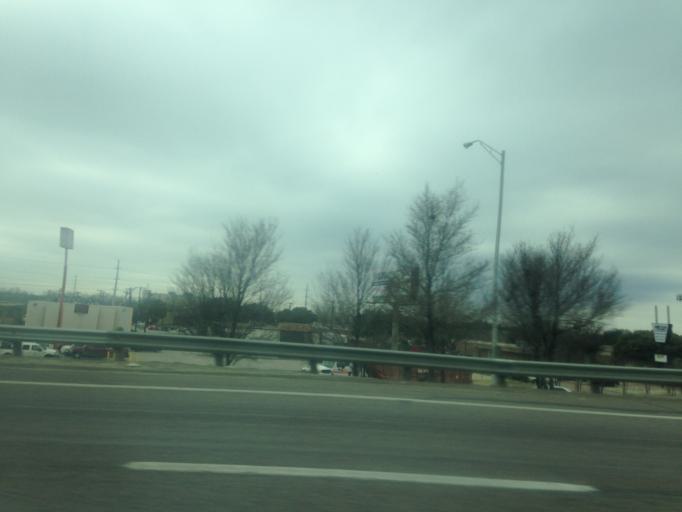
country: US
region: Texas
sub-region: Dallas County
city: Dallas
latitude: 32.8163
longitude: -96.8682
